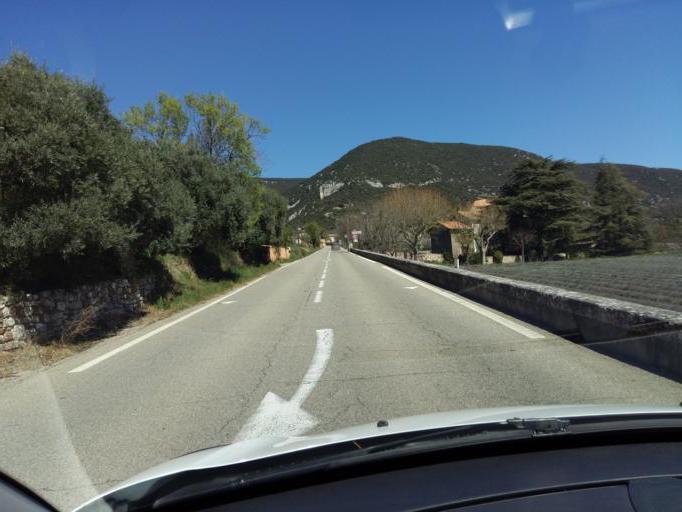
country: FR
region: Provence-Alpes-Cote d'Azur
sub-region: Departement du Vaucluse
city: Saignon
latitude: 43.9209
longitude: 5.4813
